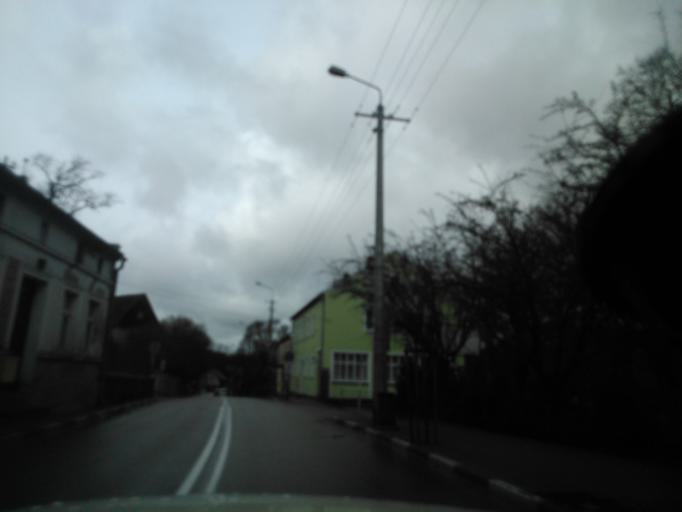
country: PL
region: Warmian-Masurian Voivodeship
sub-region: Powiat dzialdowski
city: Lidzbark
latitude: 53.2659
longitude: 19.8207
